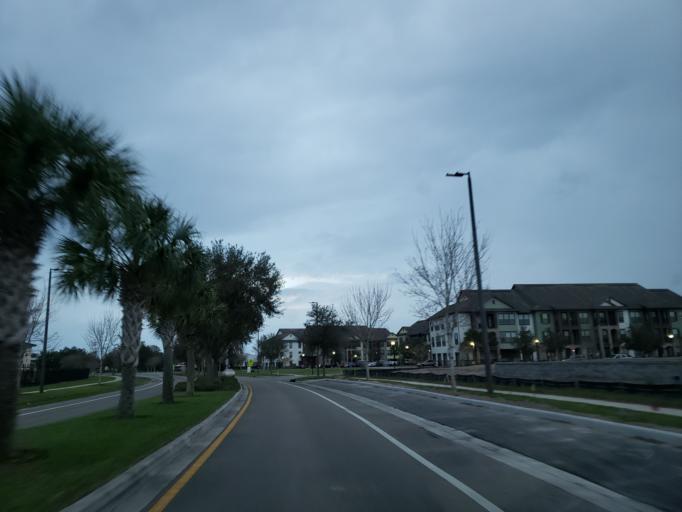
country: US
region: Florida
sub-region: Hillsborough County
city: Fish Hawk
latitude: 27.8498
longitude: -82.2564
